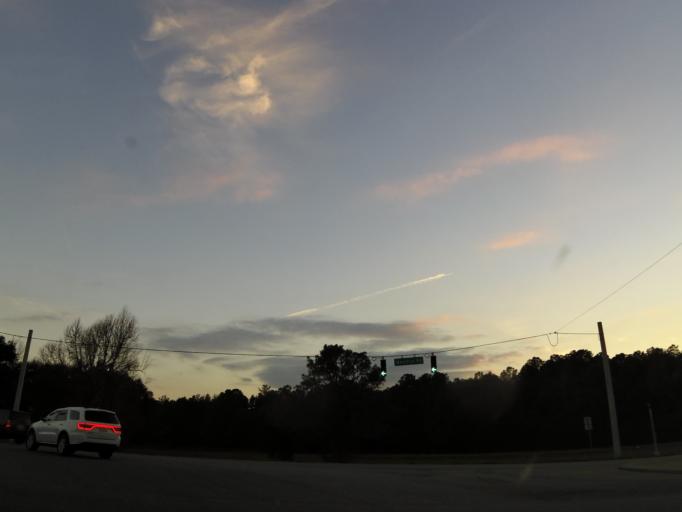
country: US
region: Georgia
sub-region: Dougherty County
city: Albany
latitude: 31.5476
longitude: -84.1173
